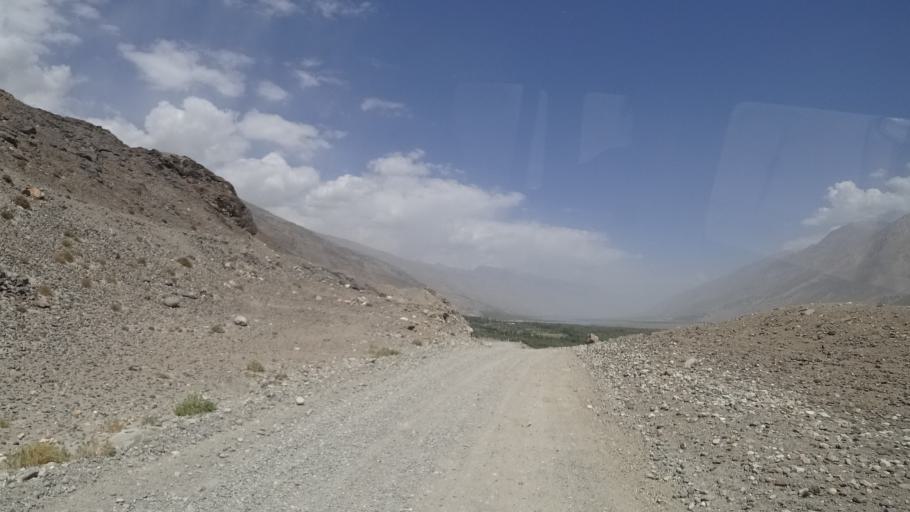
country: AF
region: Badakhshan
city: Khandud
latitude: 36.9067
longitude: 72.1693
